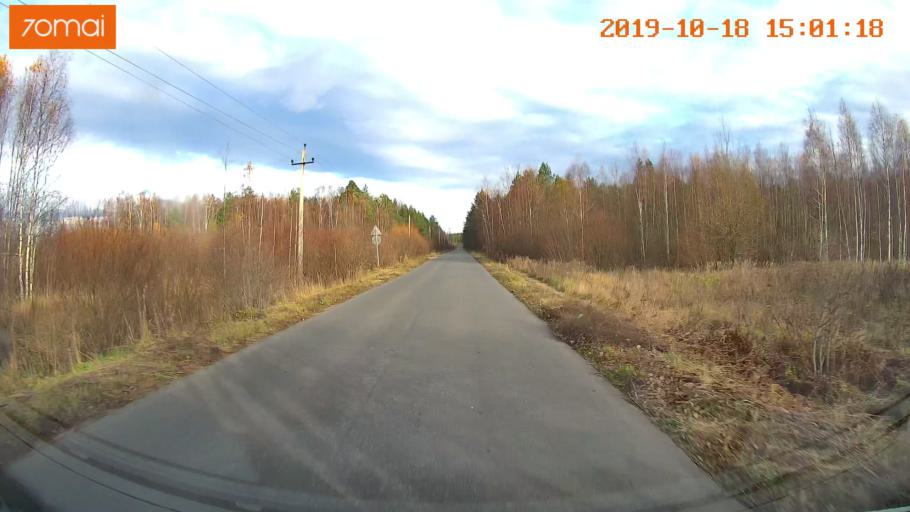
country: RU
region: Vladimir
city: Gus'-Khrustal'nyy
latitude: 55.4997
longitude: 40.5996
